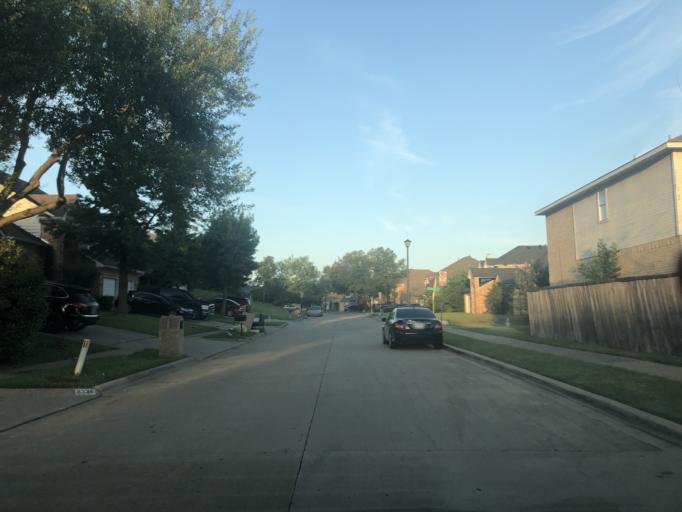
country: US
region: Texas
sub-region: Dallas County
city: Duncanville
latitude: 32.6510
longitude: -96.9708
